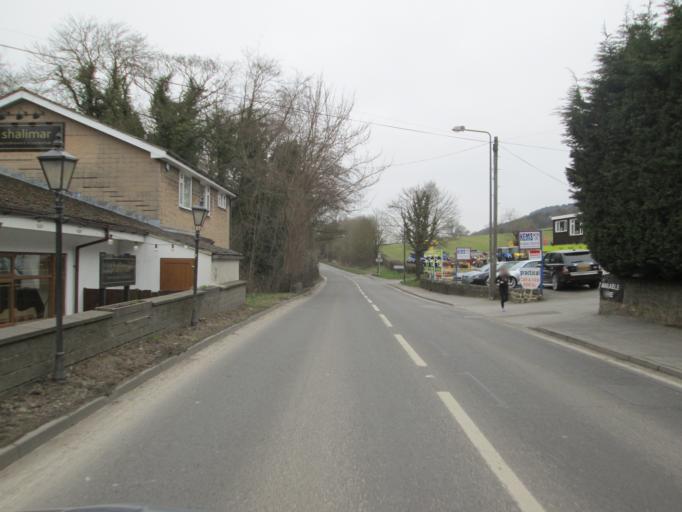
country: GB
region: England
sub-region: Derbyshire
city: Matlock
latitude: 53.1780
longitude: -1.6097
